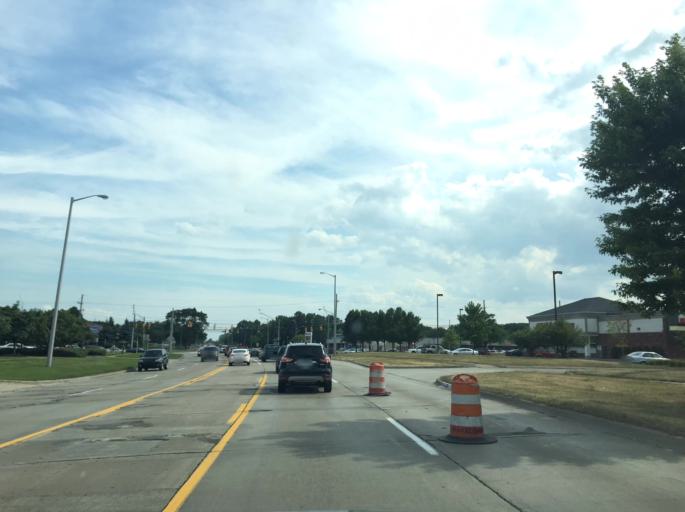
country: US
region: Michigan
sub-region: Macomb County
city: Fraser
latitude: 42.5536
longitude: -82.9897
